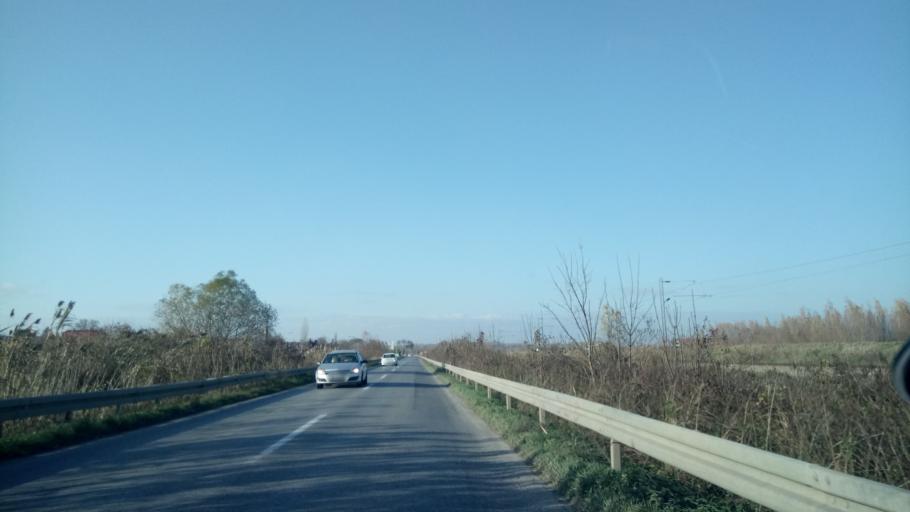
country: RS
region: Autonomna Pokrajina Vojvodina
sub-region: Juznobacki Okrug
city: Sremski Karlovci
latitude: 45.2010
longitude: 19.9415
